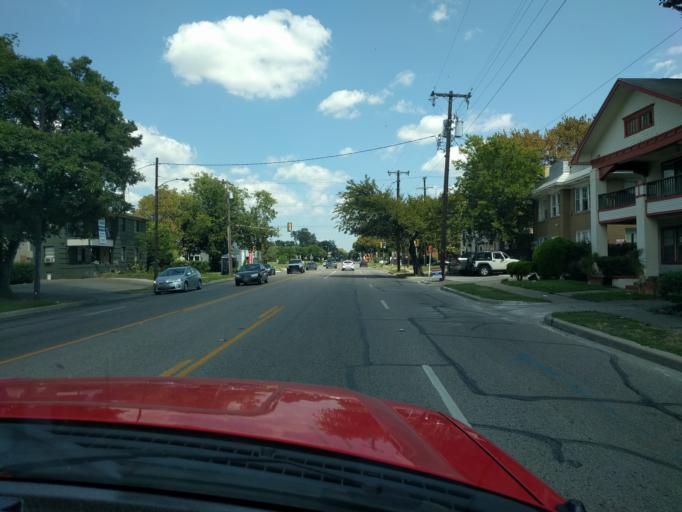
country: US
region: Texas
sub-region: Dallas County
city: Highland Park
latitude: 32.8022
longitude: -96.7729
